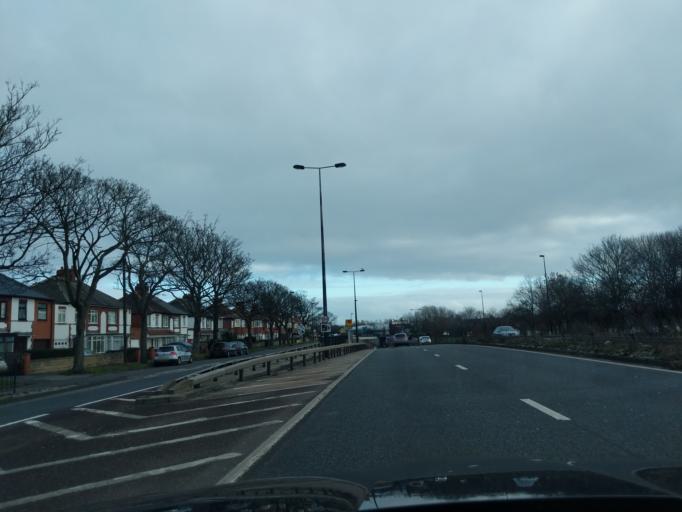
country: GB
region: England
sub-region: Borough of North Tyneside
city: Wallsend
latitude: 54.9940
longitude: -1.5710
